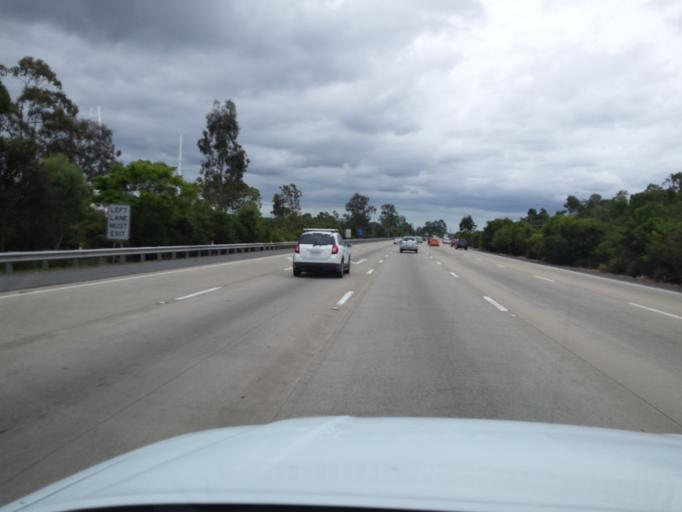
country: AU
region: Queensland
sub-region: Gold Coast
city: Upper Coomera
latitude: -27.9155
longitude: 153.3202
